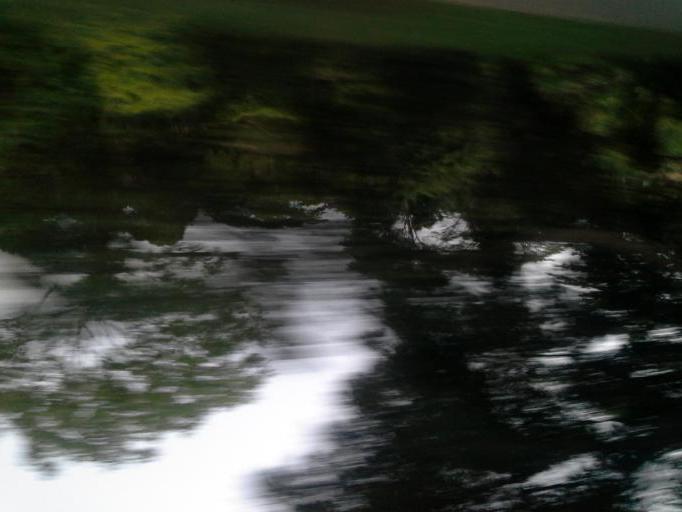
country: CO
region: Sucre
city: Los Palmitos
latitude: 9.3778
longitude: -75.2717
